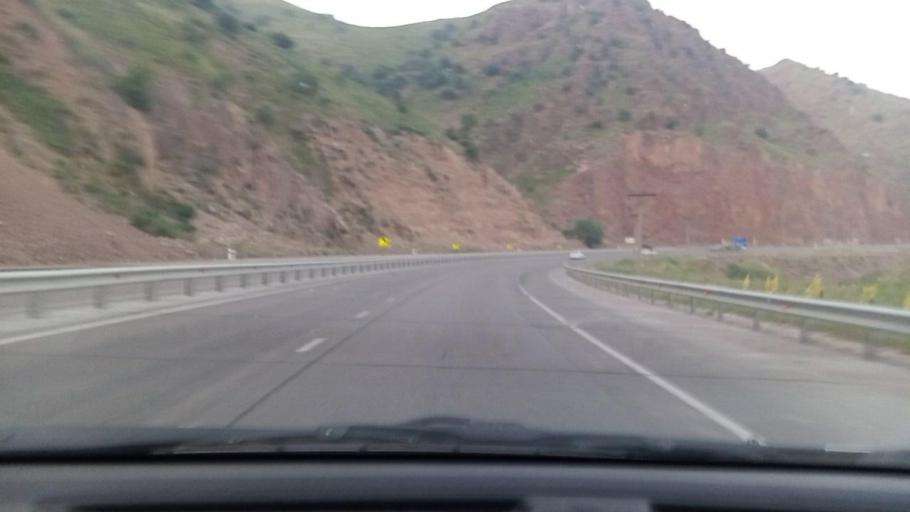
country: UZ
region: Toshkent
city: Angren
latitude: 41.1395
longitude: 70.3836
